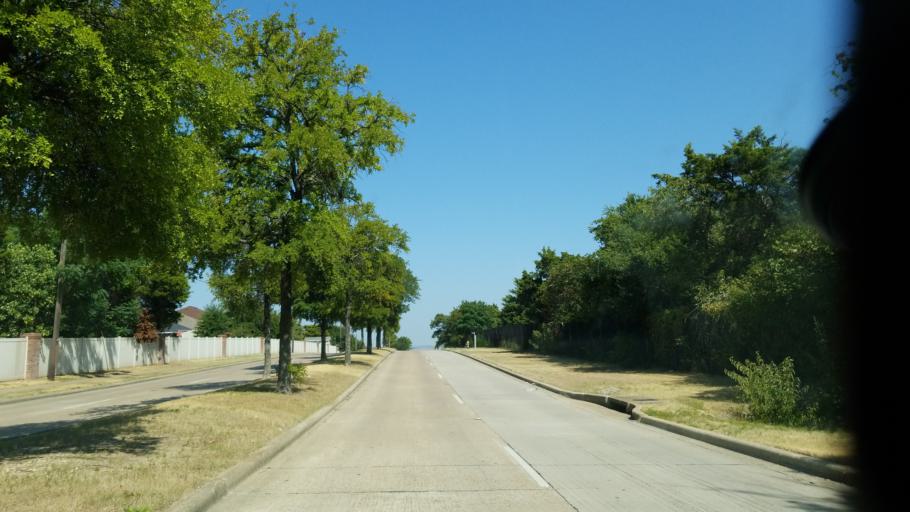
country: US
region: Texas
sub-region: Dallas County
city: Cockrell Hill
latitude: 32.7326
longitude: -96.9129
